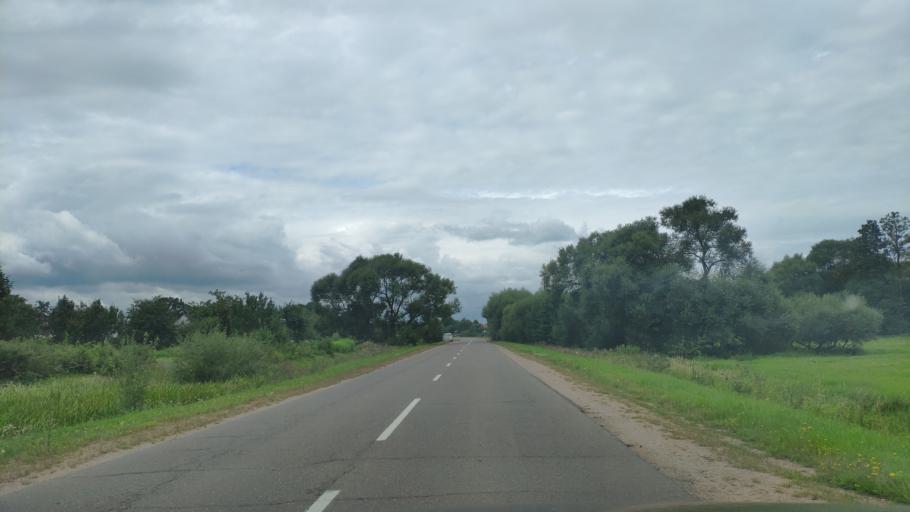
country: BY
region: Minsk
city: Khatsyezhyna
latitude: 53.8839
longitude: 27.2658
